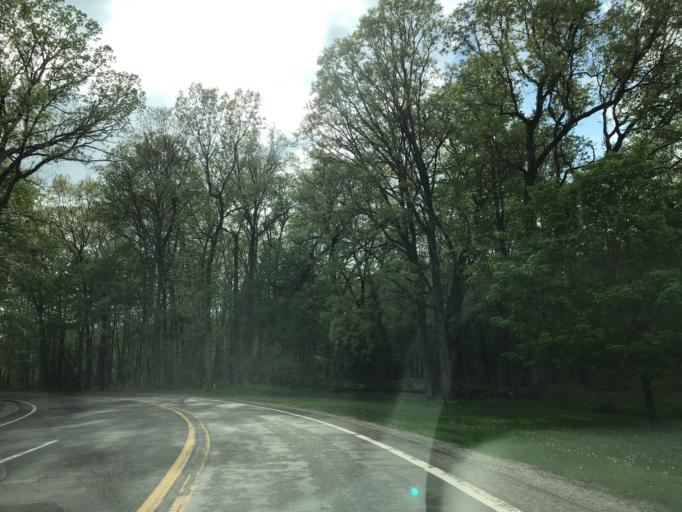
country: US
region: Michigan
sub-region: Oakland County
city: South Lyon
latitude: 42.5342
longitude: -83.6600
